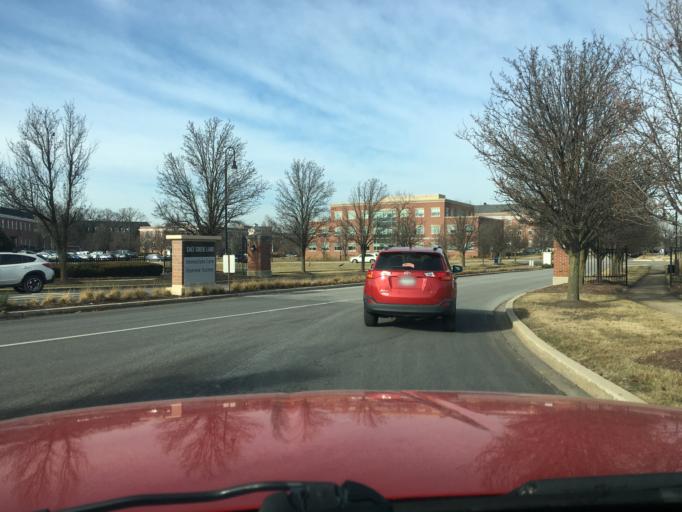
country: US
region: Illinois
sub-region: DuPage County
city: Oak Brook
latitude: 41.8177
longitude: -87.9207
